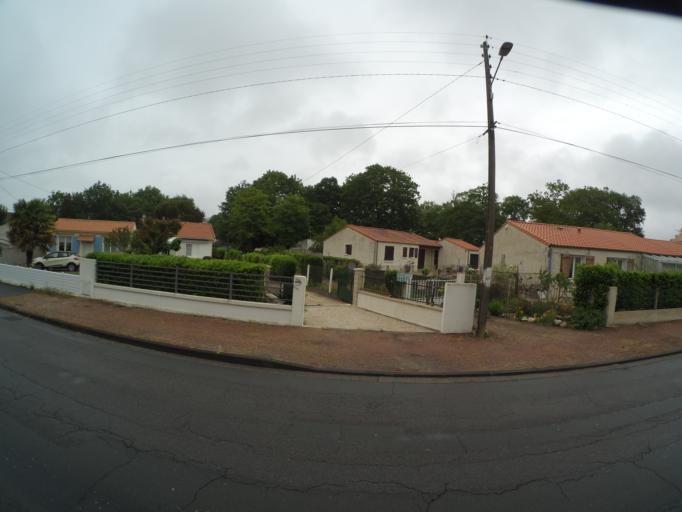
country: FR
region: Poitou-Charentes
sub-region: Departement de la Charente-Maritime
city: Saint-Georges-de-Didonne
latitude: 45.6112
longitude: -0.9971
